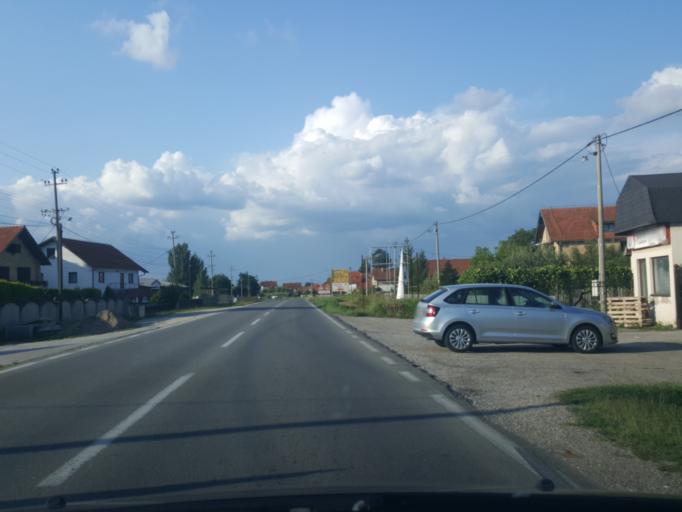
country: RS
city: Lipnicki Sor
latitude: 44.5852
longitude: 19.2567
